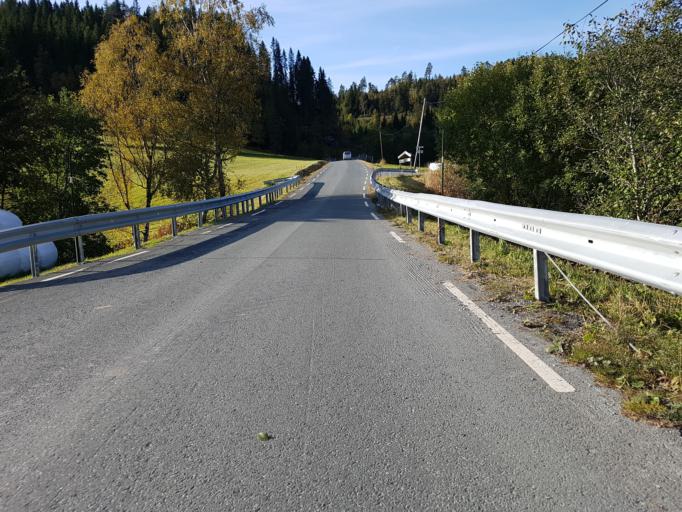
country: NO
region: Sor-Trondelag
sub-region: Klaebu
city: Klaebu
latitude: 63.3451
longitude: 10.5425
